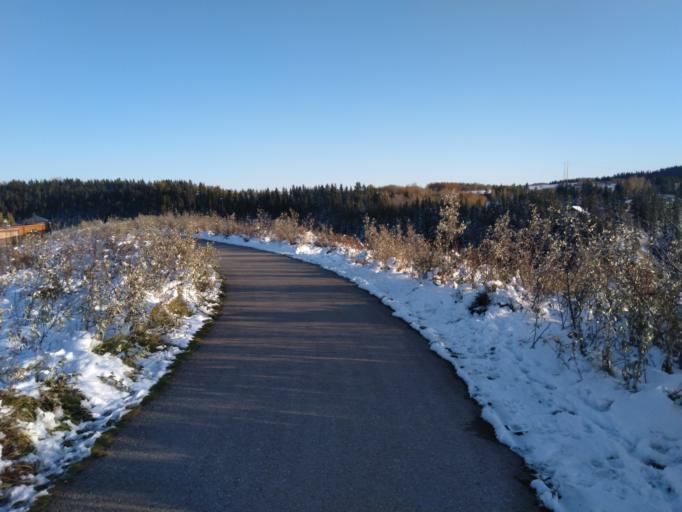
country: CA
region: Alberta
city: Cochrane
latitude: 51.1818
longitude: -114.5071
